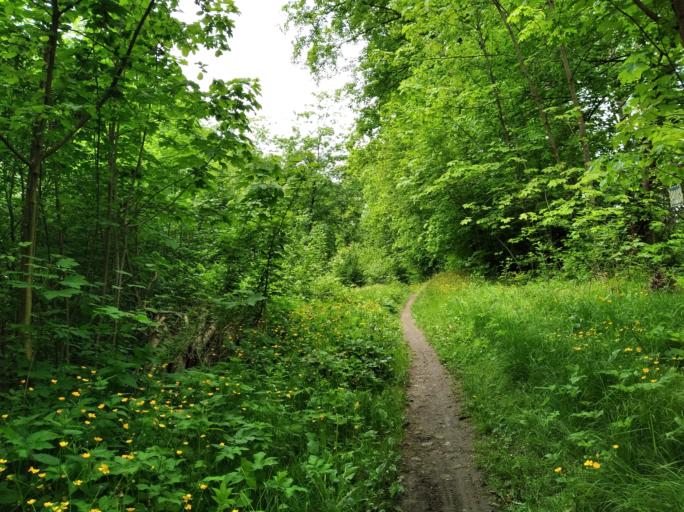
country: PL
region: Subcarpathian Voivodeship
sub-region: Powiat strzyzowski
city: Czudec
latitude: 49.9378
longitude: 21.8371
